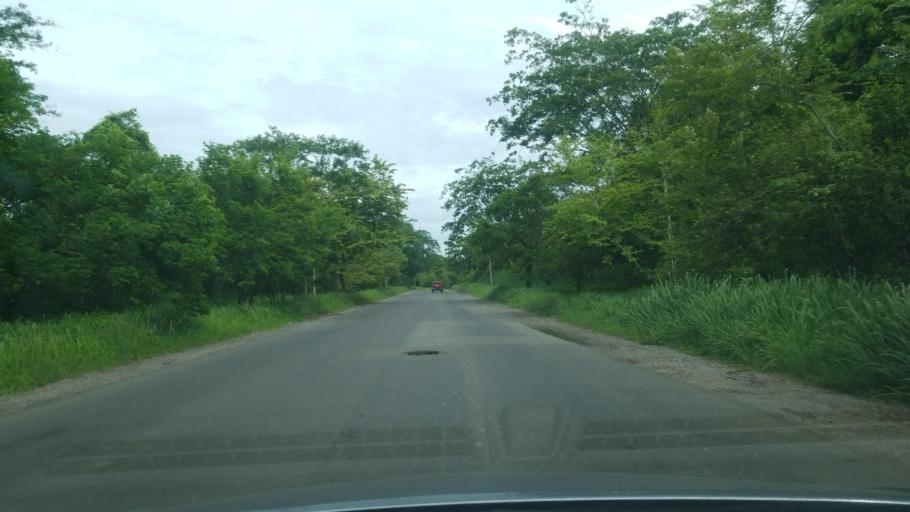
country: HN
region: Santa Barbara
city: Camalote
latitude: 15.3269
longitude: -88.3243
